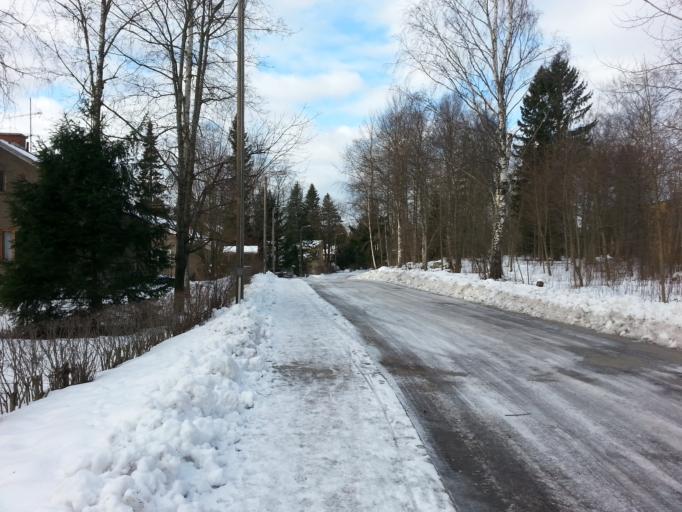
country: FI
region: Uusimaa
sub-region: Helsinki
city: Teekkarikylae
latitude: 60.2353
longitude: 24.8431
